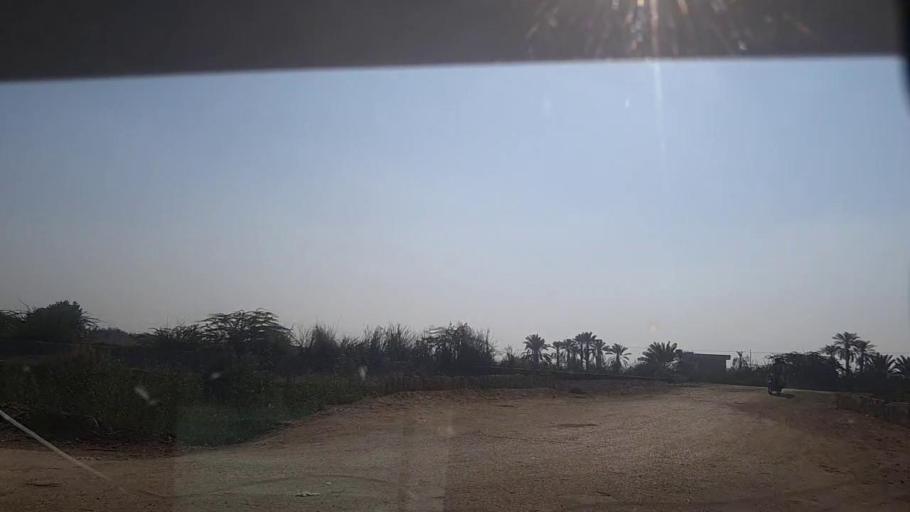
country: PK
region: Sindh
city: Gambat
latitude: 27.3630
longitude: 68.5570
